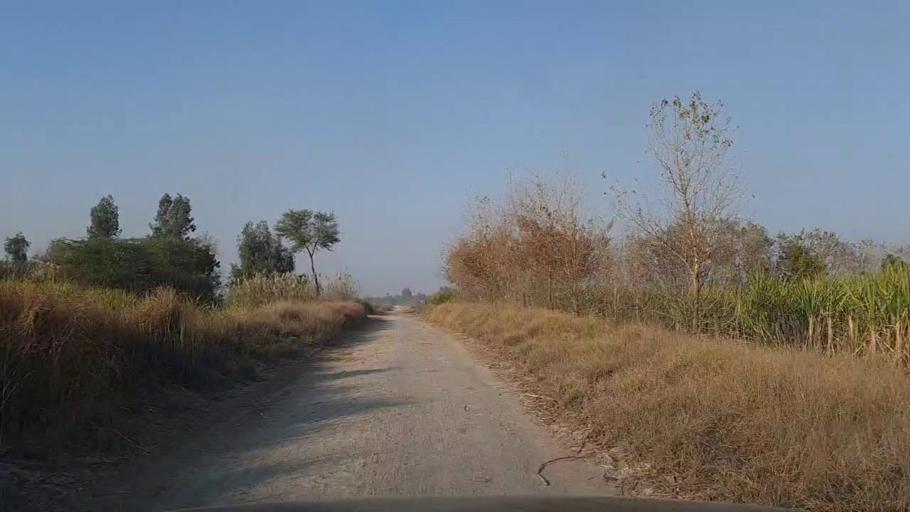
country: PK
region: Sindh
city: Daur
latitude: 26.4587
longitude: 68.4380
